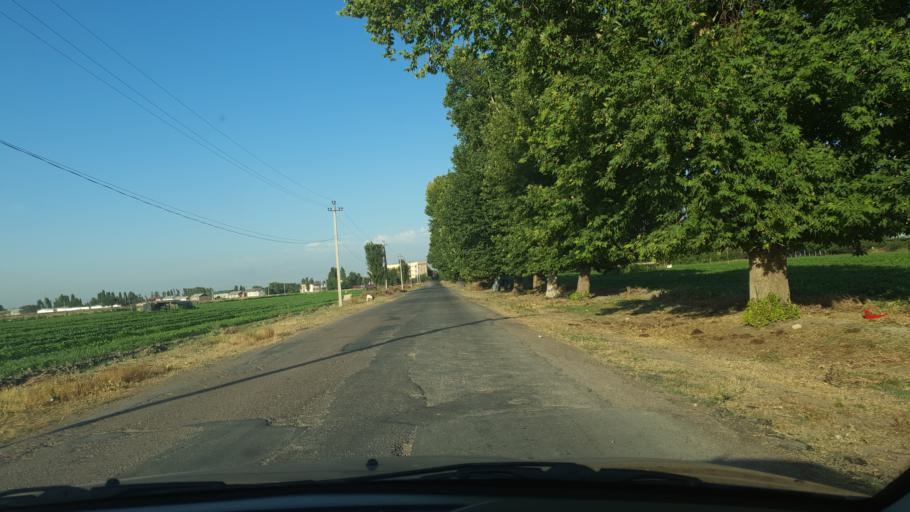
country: UZ
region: Toshkent
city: Tuytepa
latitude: 41.0862
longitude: 69.3482
